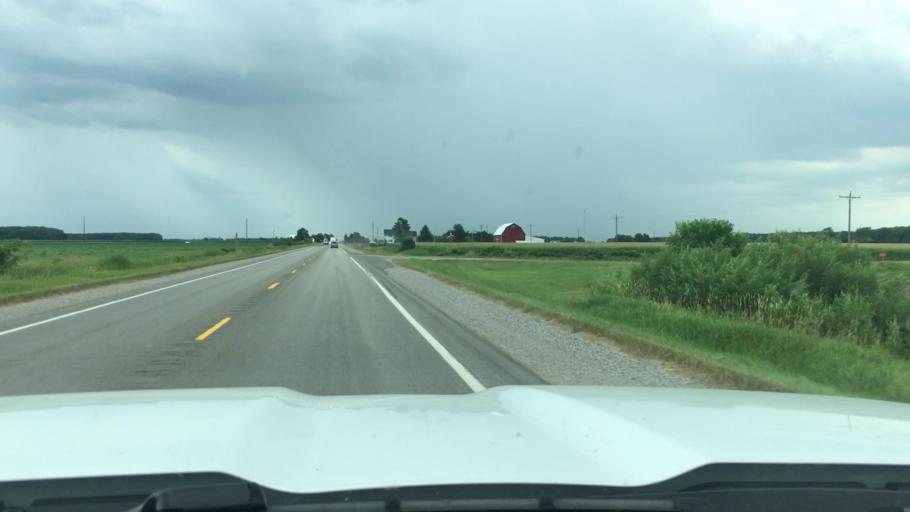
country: US
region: Michigan
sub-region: Montcalm County
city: Carson City
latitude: 43.1764
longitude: -84.7891
